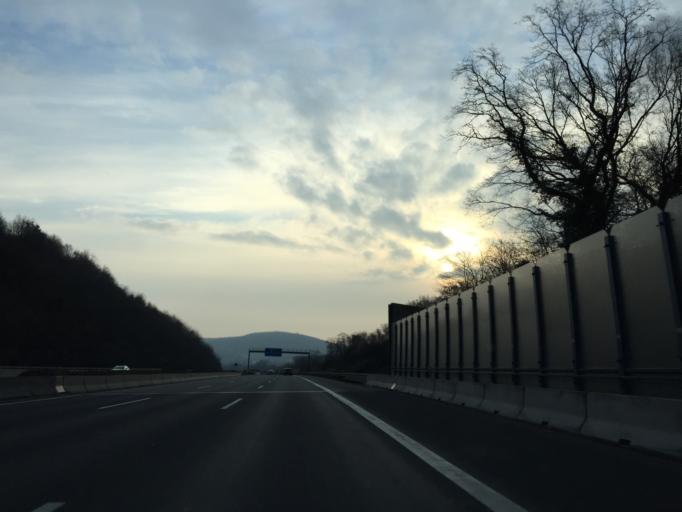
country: DE
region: Bavaria
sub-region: Regierungsbezirk Unterfranken
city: Glattbach
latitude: 49.9923
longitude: 9.1512
